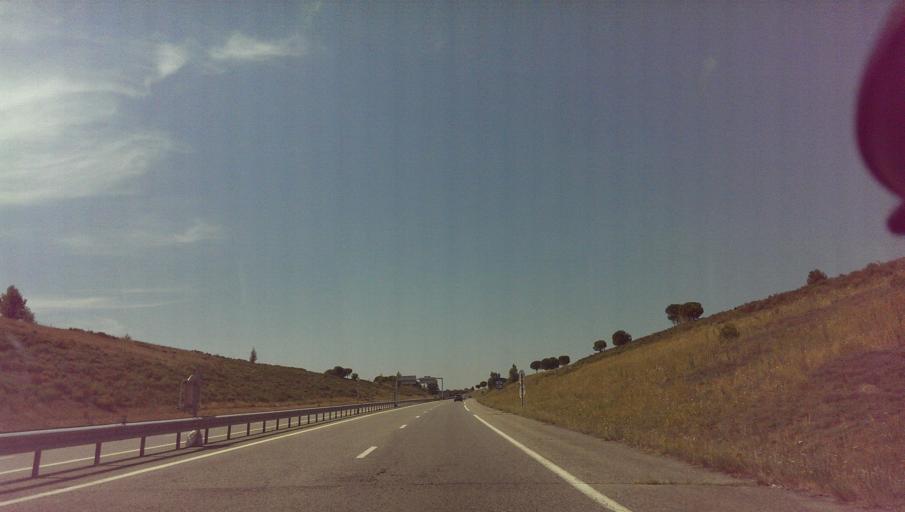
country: FR
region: Midi-Pyrenees
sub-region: Departement de la Haute-Garonne
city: Villenouvelle
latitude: 43.4067
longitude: 1.6477
